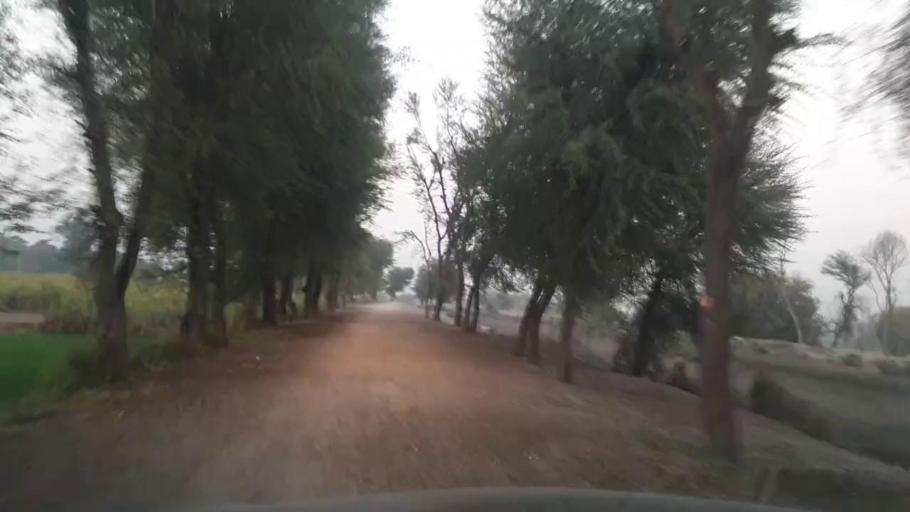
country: PK
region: Sindh
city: Ubauro
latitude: 28.1844
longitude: 69.7815
